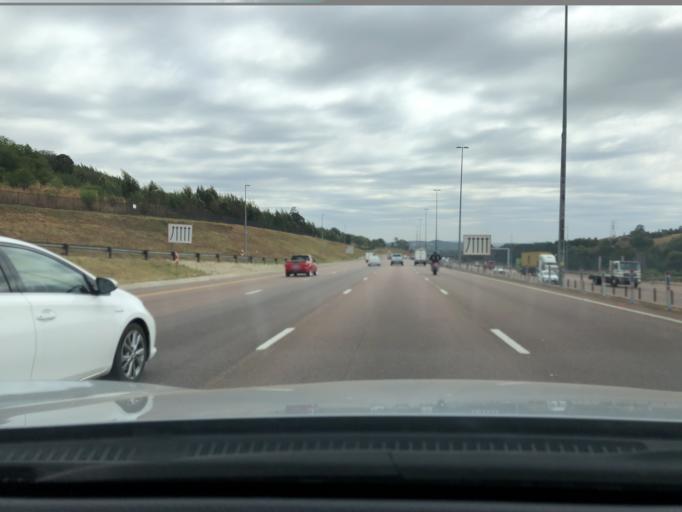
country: ZA
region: Gauteng
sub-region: City of Tshwane Metropolitan Municipality
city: Centurion
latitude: -25.8078
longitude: 28.2590
